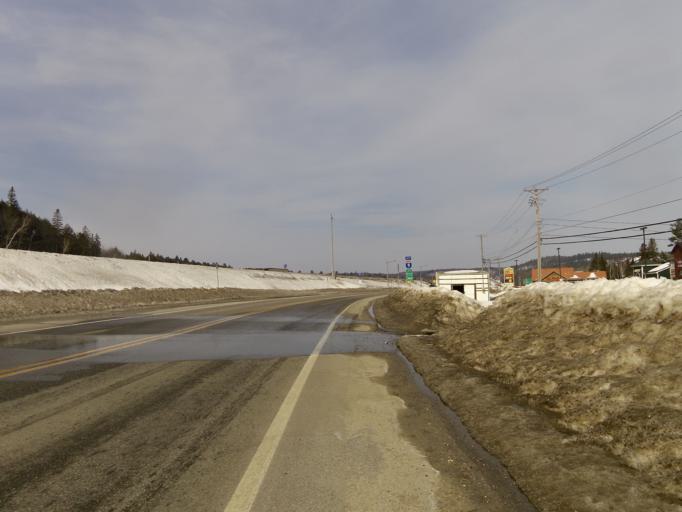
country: CA
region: Quebec
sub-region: Outaouais
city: Wakefield
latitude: 45.6236
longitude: -75.9337
